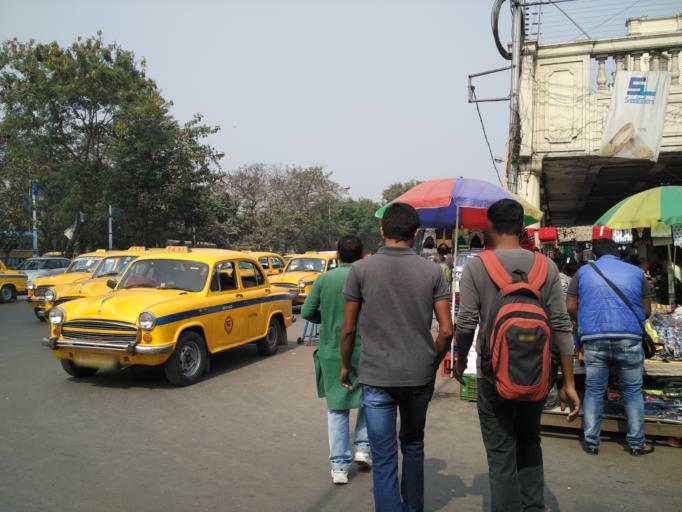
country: IN
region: West Bengal
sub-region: Kolkata
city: Bara Bazar
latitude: 22.5607
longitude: 88.3509
